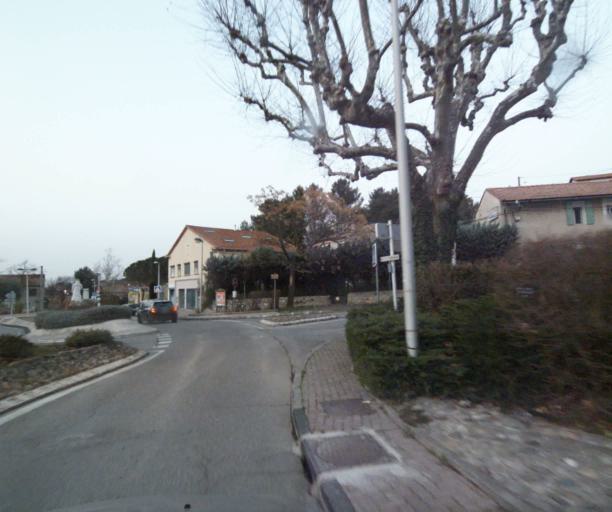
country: FR
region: Provence-Alpes-Cote d'Azur
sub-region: Departement des Bouches-du-Rhone
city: Gardanne
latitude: 43.4334
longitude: 5.4665
